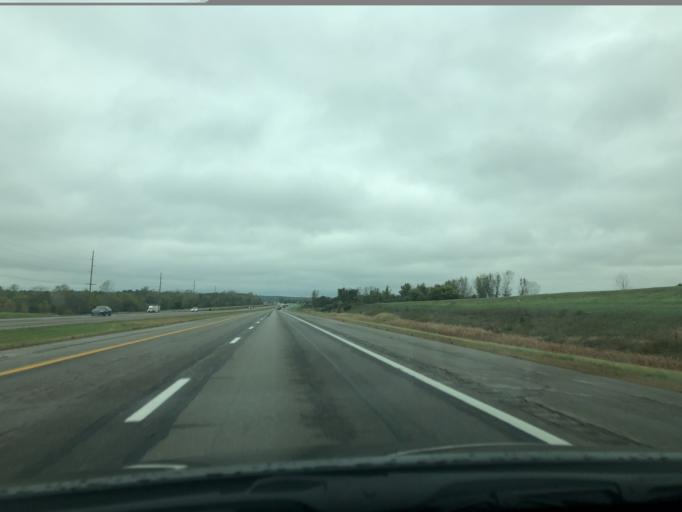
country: US
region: Ohio
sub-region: Champaign County
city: North Lewisburg
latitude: 40.3041
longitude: -83.5649
